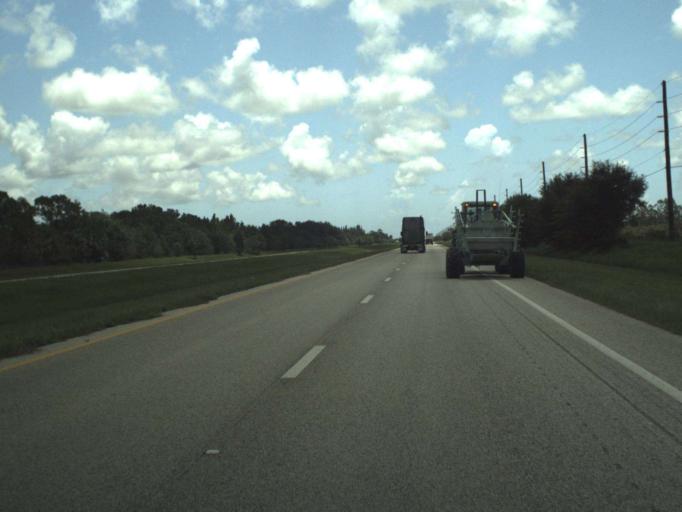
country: US
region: Florida
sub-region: Indian River County
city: West Vero Corridor
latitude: 27.6395
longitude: -80.5673
